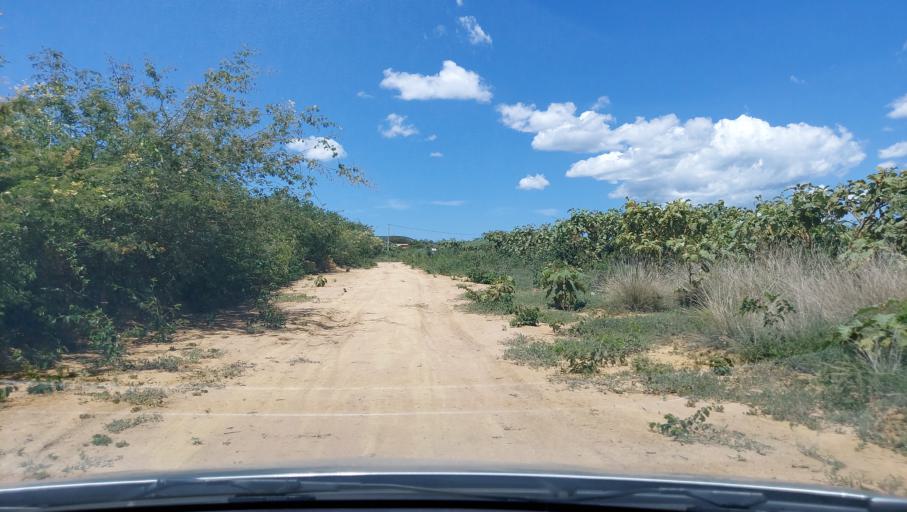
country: BR
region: Bahia
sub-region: Oliveira Dos Brejinhos
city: Beira Rio
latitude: -12.0078
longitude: -42.6351
